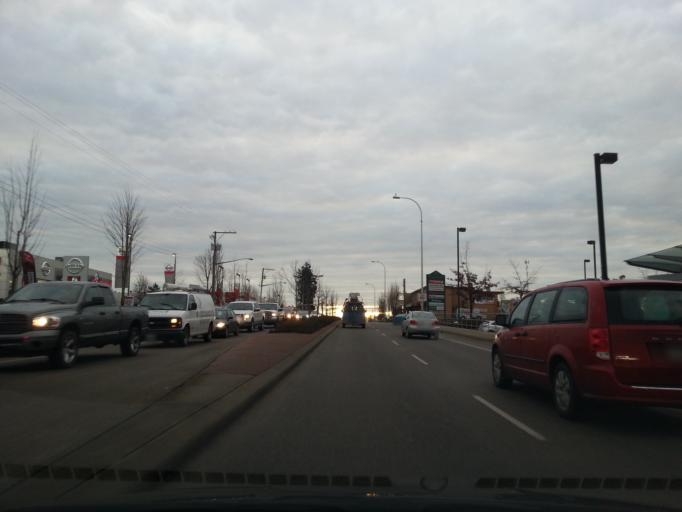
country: CA
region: British Columbia
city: Surrey
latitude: 49.1657
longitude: -122.8006
